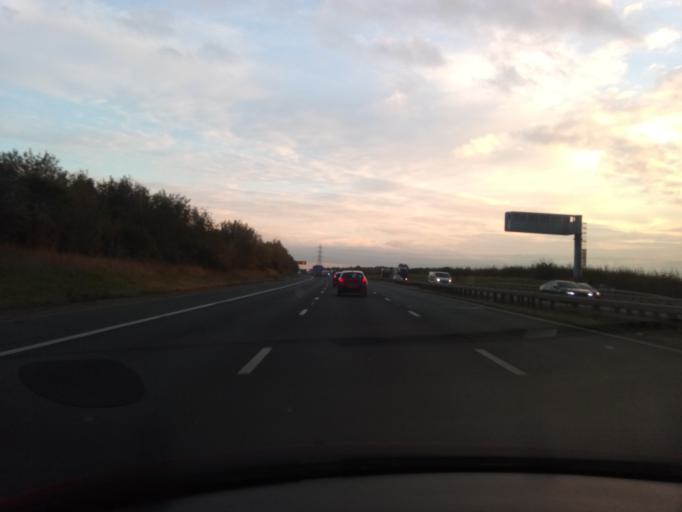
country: GB
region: England
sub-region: City and Borough of Leeds
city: Wetherby
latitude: 53.9622
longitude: -1.3708
